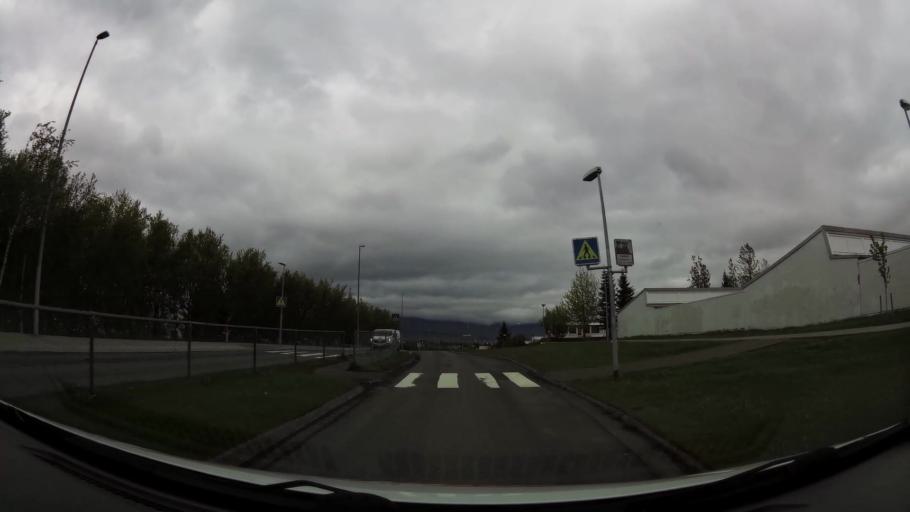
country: IS
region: Capital Region
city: Reykjavik
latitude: 64.1235
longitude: -21.8672
